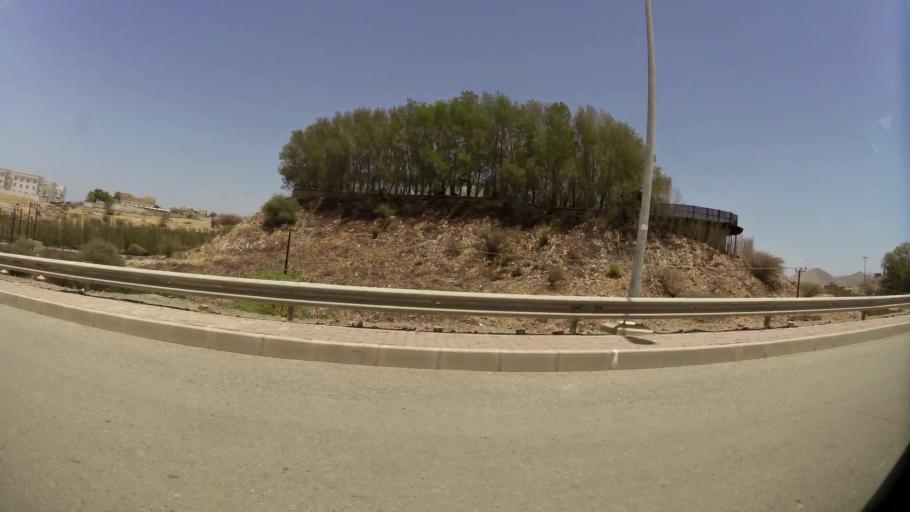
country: OM
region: Muhafazat Masqat
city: Bawshar
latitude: 23.6072
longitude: 58.4787
